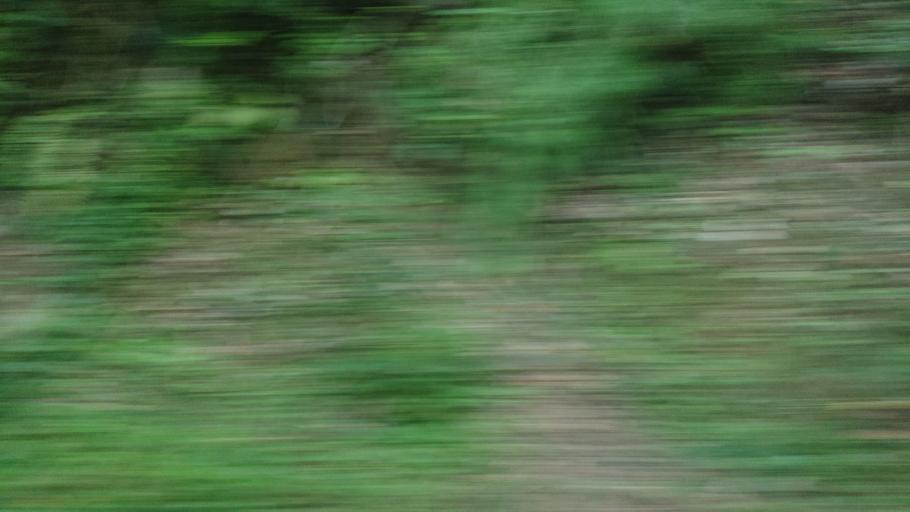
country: TW
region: Taiwan
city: Daxi
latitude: 24.8839
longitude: 121.3787
